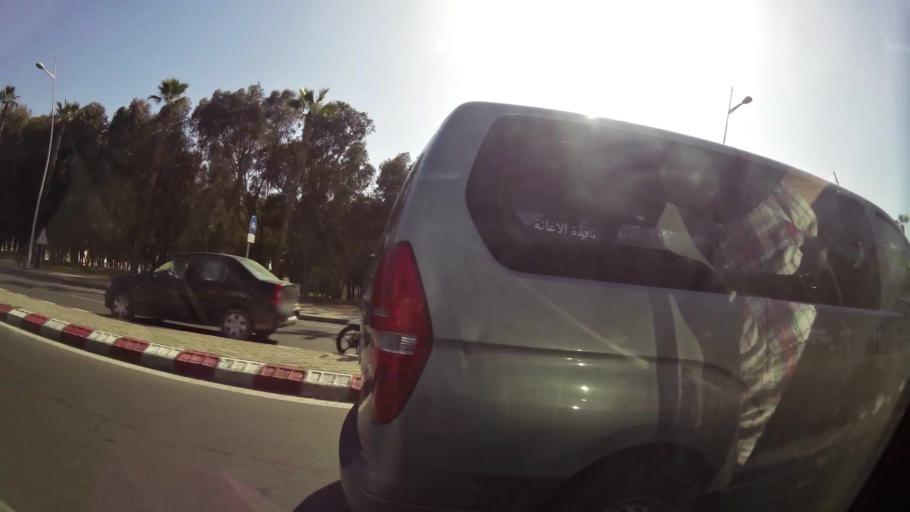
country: MA
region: Oued ed Dahab-Lagouira
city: Dakhla
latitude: 30.3881
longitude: -9.5743
